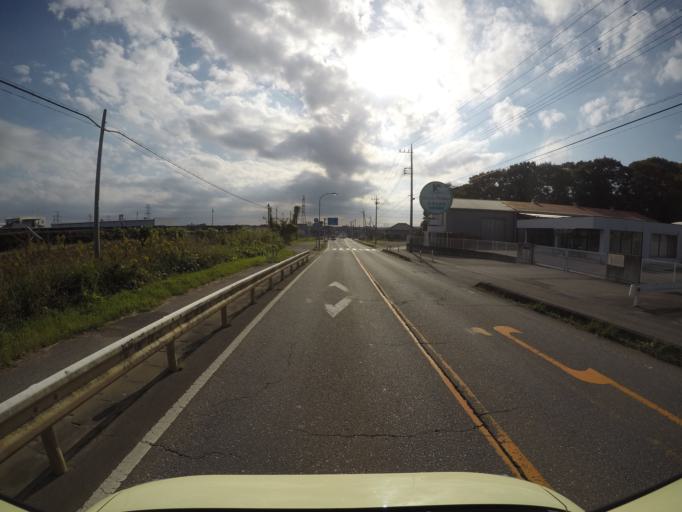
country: JP
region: Ibaraki
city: Iwai
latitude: 35.9934
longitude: 139.9020
